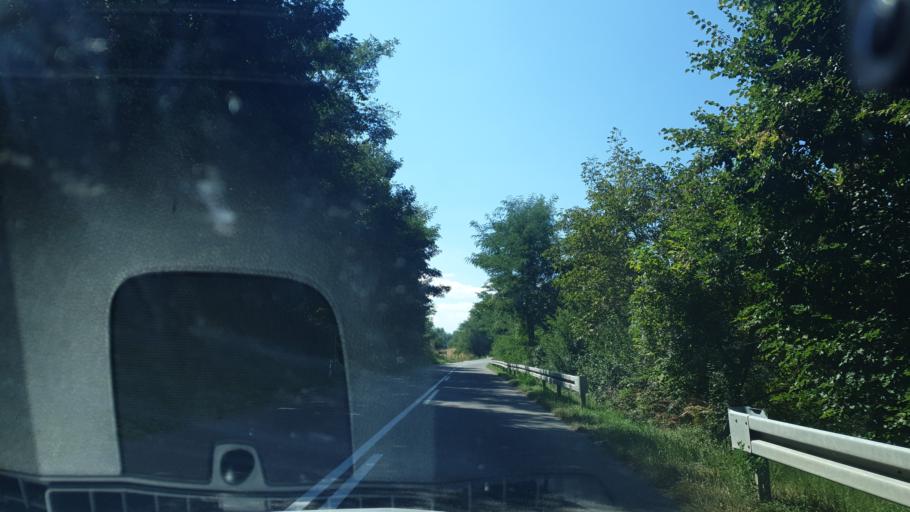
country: RS
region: Central Serbia
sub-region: Kolubarski Okrug
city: Mionica
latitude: 44.1753
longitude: 20.0115
